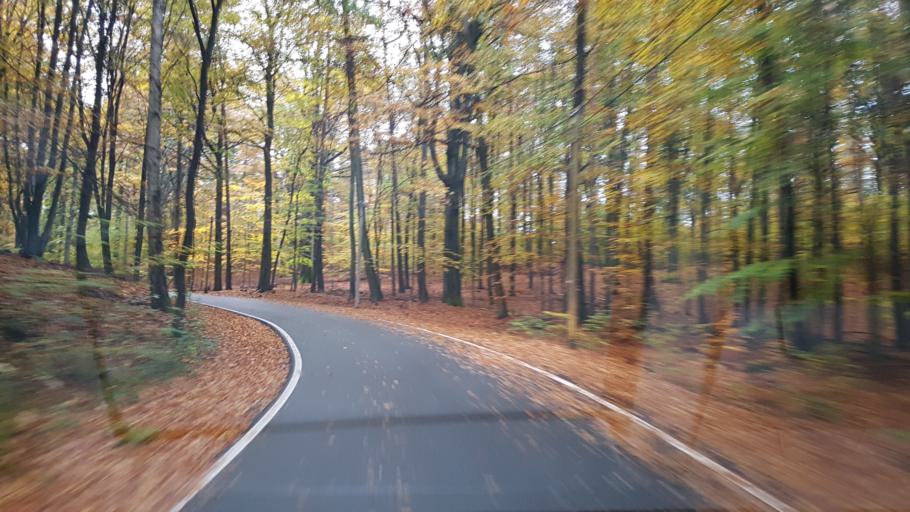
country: DE
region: Saxony
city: Cavertitz
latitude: 51.4111
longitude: 13.0667
